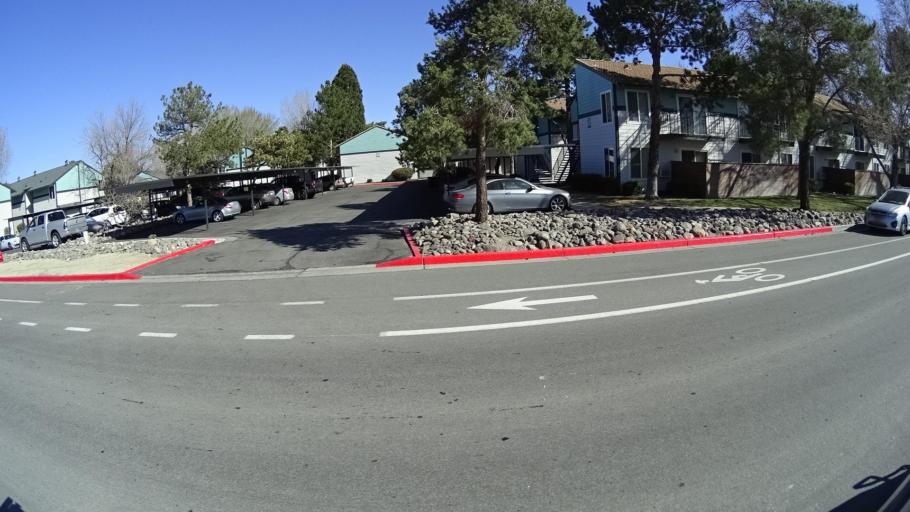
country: US
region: Nevada
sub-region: Washoe County
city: Reno
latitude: 39.4696
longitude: -119.7792
